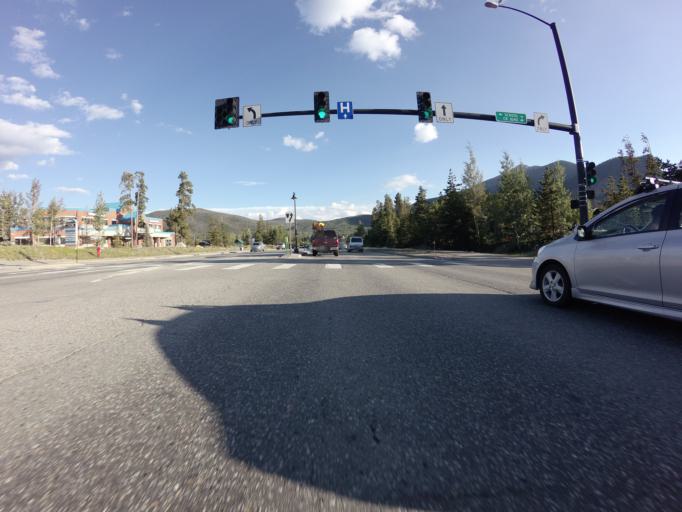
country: US
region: Colorado
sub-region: Summit County
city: Frisco
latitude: 39.5817
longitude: -106.0936
